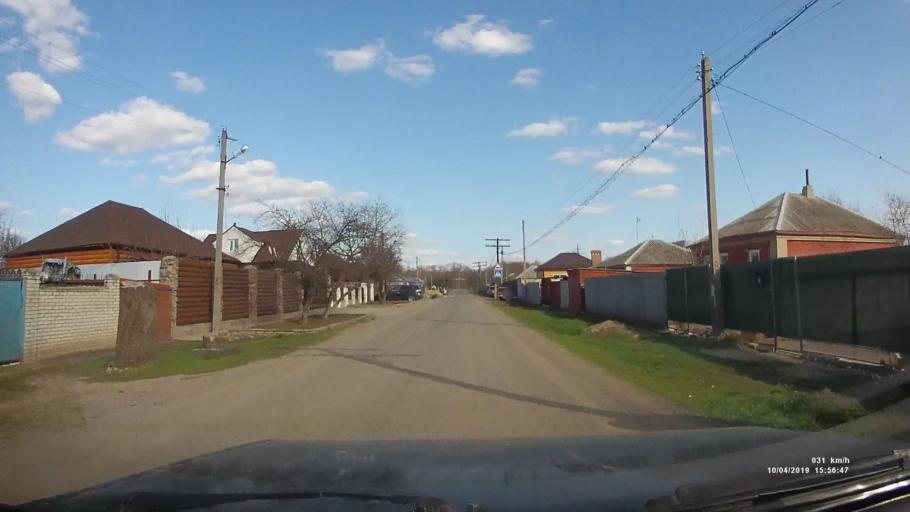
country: RU
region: Rostov
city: Masalovka
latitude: 48.4110
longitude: 40.2717
